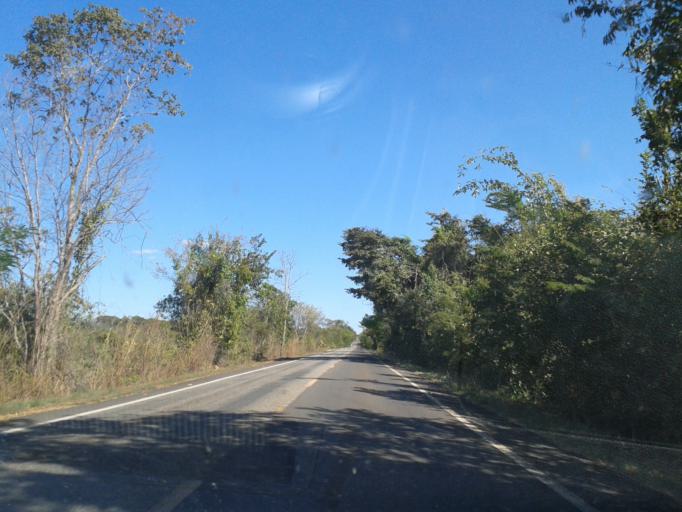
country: BR
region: Goias
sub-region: Crixas
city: Crixas
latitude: -13.9952
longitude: -50.3241
